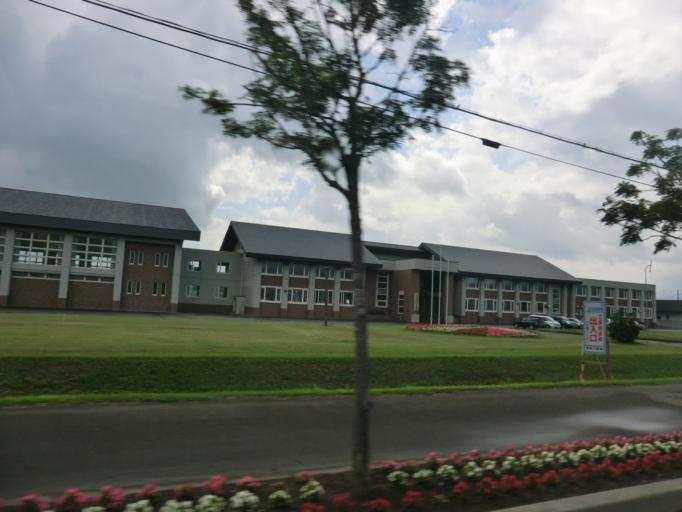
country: JP
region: Hokkaido
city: Fukagawa
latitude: 44.0060
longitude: 142.1490
